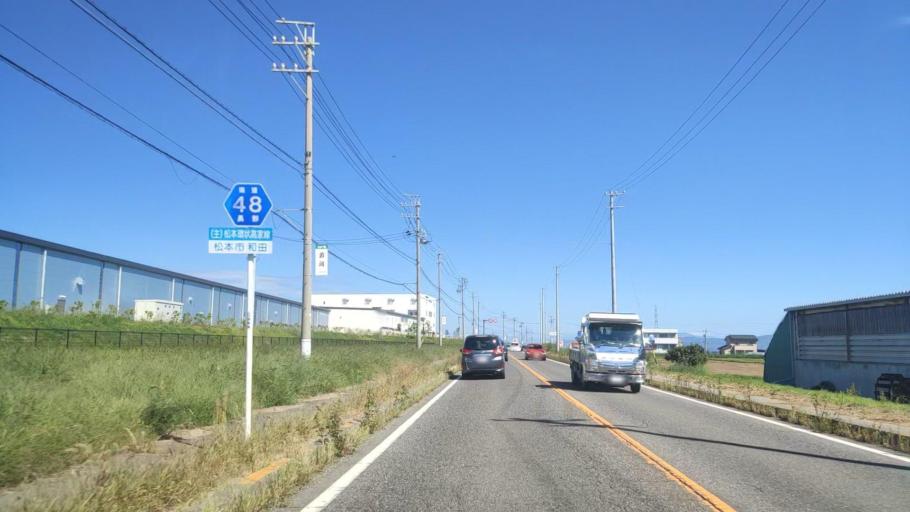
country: JP
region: Nagano
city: Matsumoto
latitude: 36.1913
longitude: 137.9031
